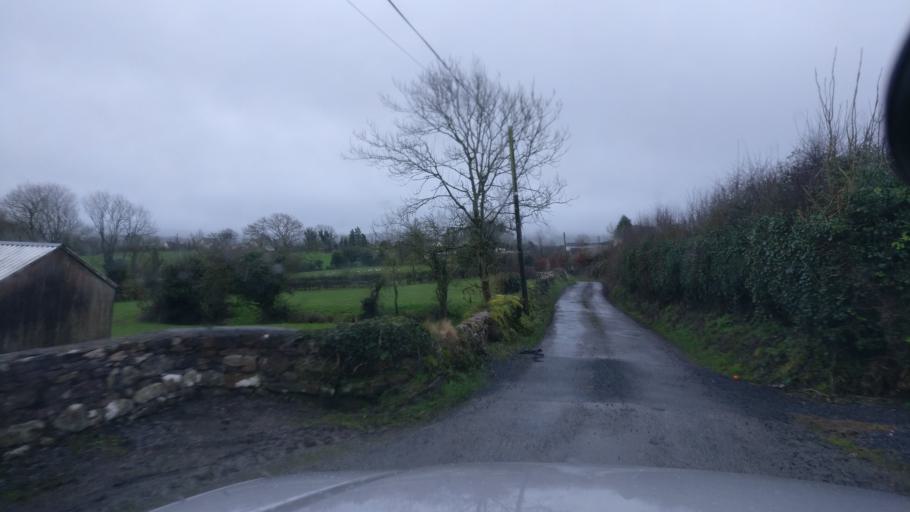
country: IE
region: Connaught
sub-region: County Galway
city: Loughrea
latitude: 53.1640
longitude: -8.6413
